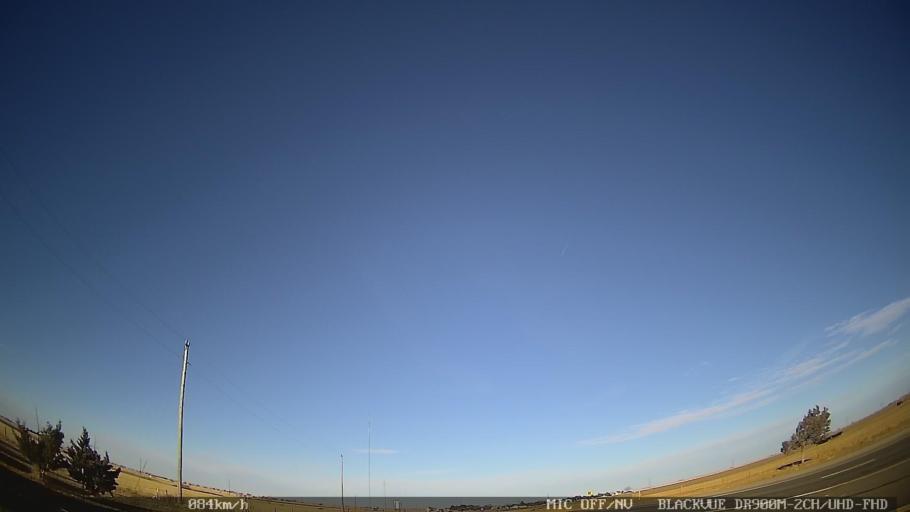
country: US
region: New Mexico
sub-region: Curry County
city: Clovis
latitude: 34.4340
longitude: -103.2424
